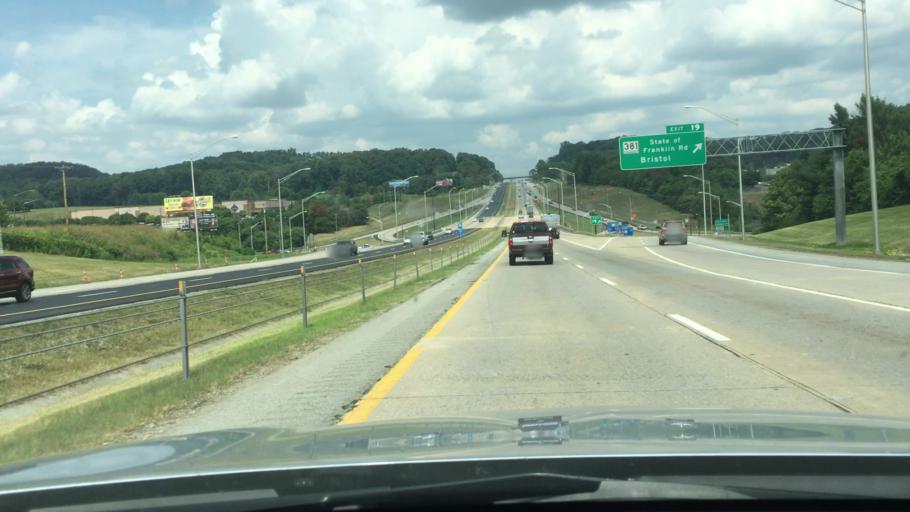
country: US
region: Tennessee
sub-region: Washington County
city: Johnson City
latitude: 36.3534
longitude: -82.3937
